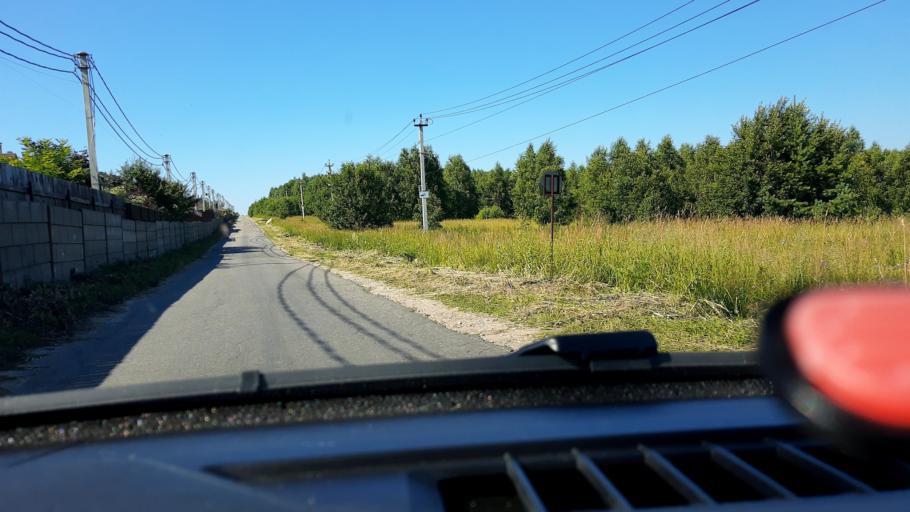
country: RU
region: Nizjnij Novgorod
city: Babino
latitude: 56.1344
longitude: 43.6407
